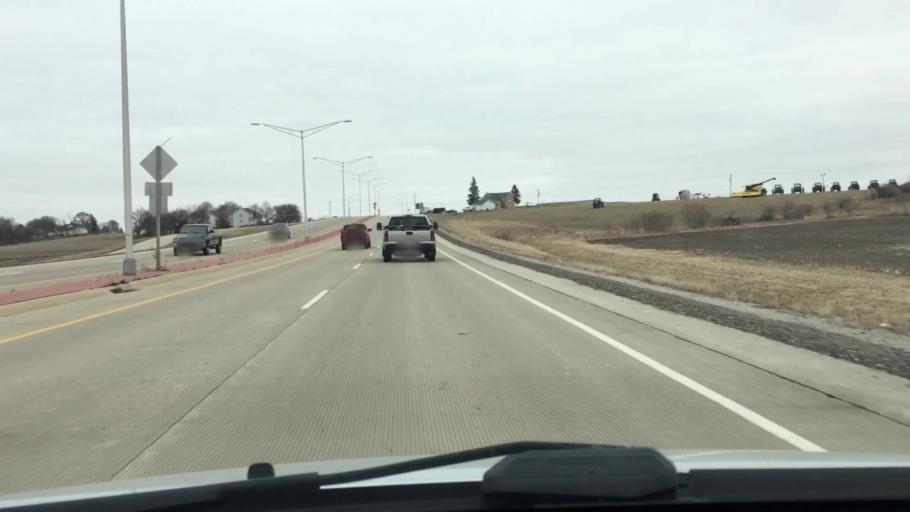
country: US
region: Wisconsin
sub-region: Jefferson County
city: Watertown
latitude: 43.1571
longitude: -88.7394
